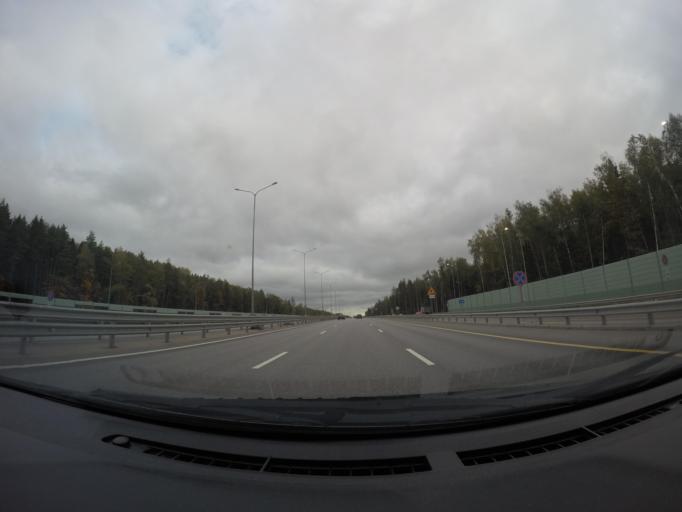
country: RU
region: Moskovskaya
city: Kubinka
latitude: 55.5768
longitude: 36.7550
